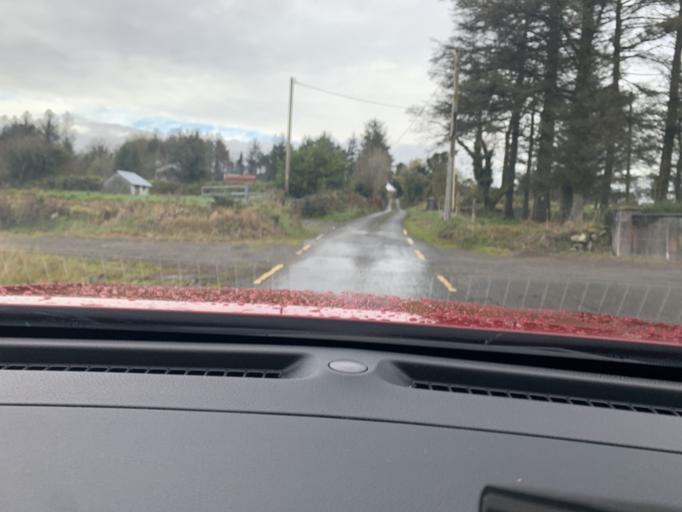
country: IE
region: Connaught
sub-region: Roscommon
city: Ballaghaderreen
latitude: 53.9164
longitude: -8.5669
